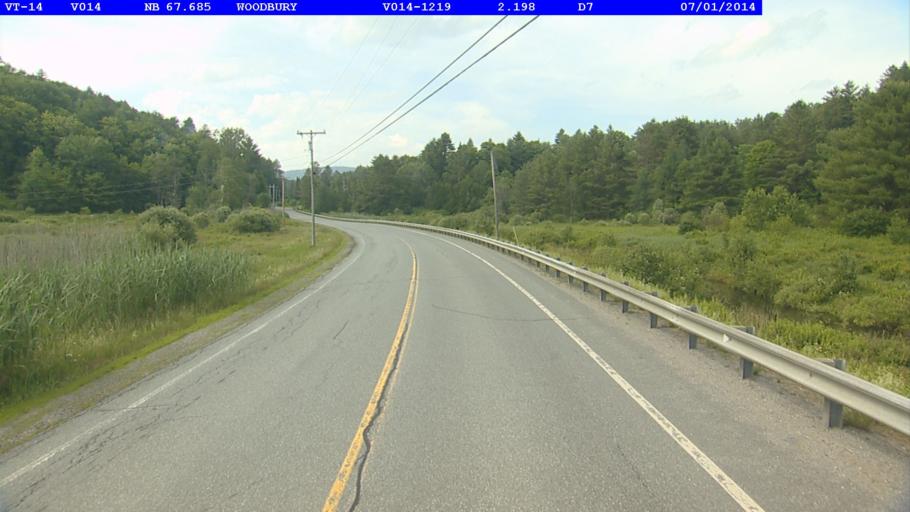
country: US
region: Vermont
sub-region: Caledonia County
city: Hardwick
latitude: 44.4202
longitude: -72.4104
